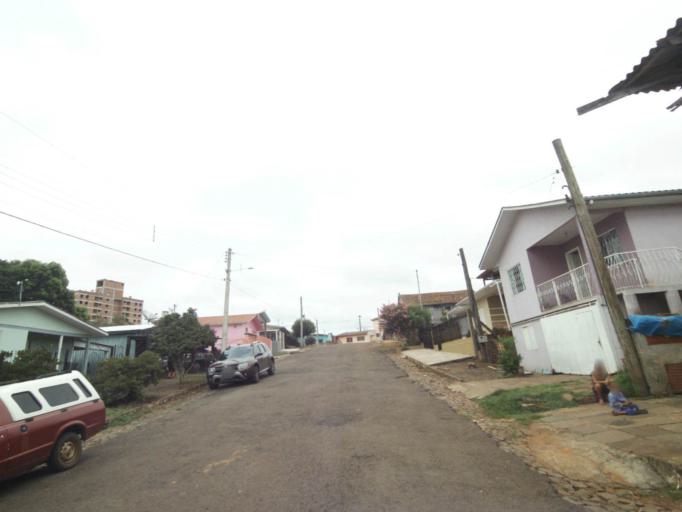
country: BR
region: Rio Grande do Sul
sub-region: Lagoa Vermelha
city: Lagoa Vermelha
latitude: -28.2119
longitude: -51.5135
